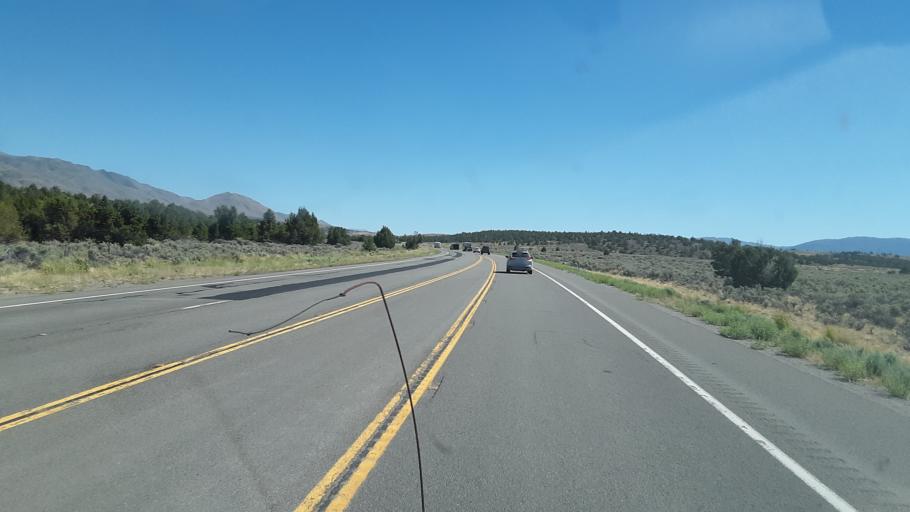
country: US
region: Nevada
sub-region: Washoe County
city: Cold Springs
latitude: 39.8506
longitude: -120.0436
